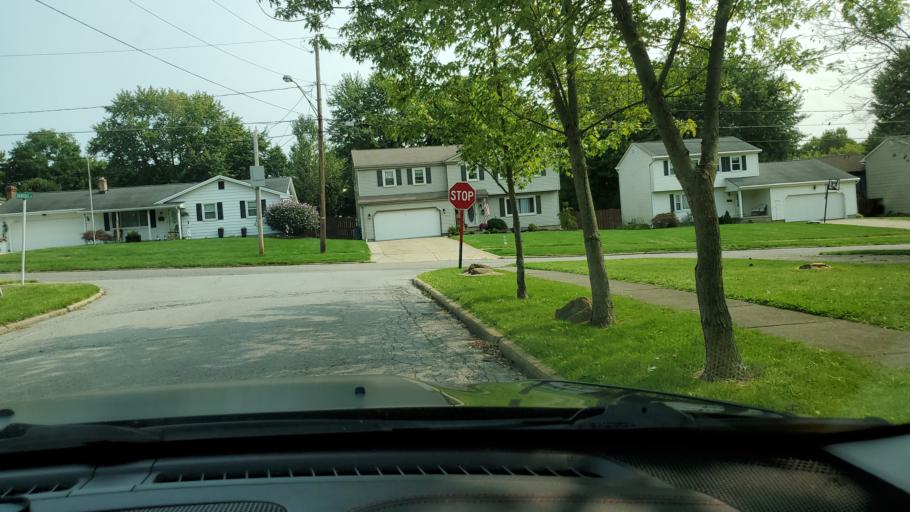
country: US
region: Ohio
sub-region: Mahoning County
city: Boardman
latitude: 41.0377
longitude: -80.6519
